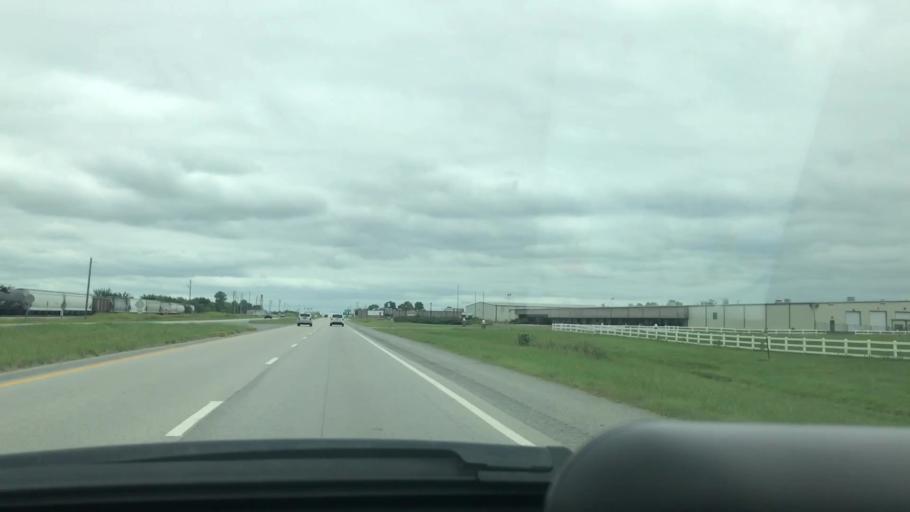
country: US
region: Oklahoma
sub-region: Mayes County
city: Chouteau
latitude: 36.2381
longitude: -95.3380
